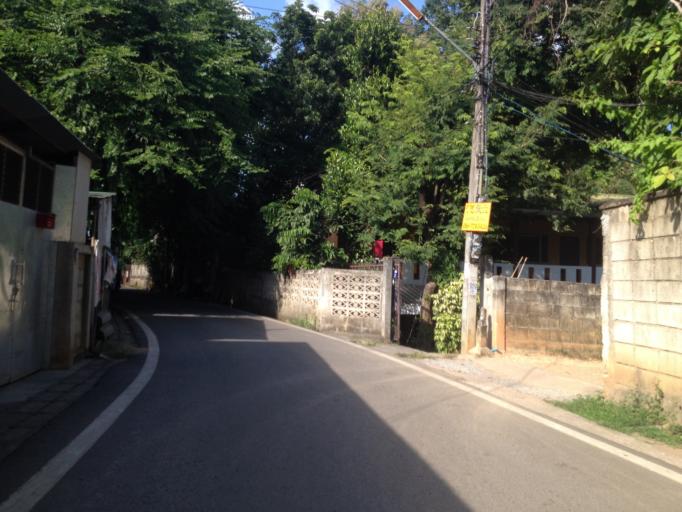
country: TH
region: Chiang Mai
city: Chiang Mai
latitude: 18.7876
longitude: 98.9509
